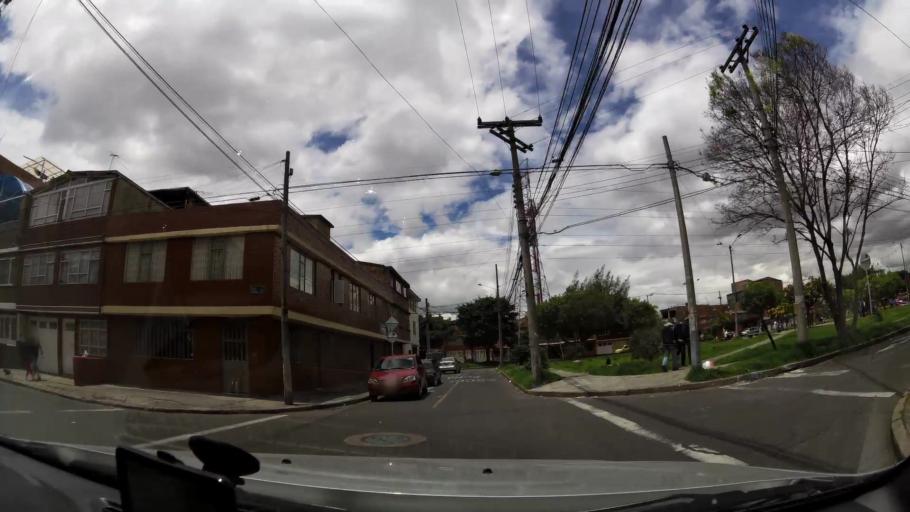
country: CO
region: Bogota D.C.
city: Bogota
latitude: 4.6133
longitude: -74.1141
